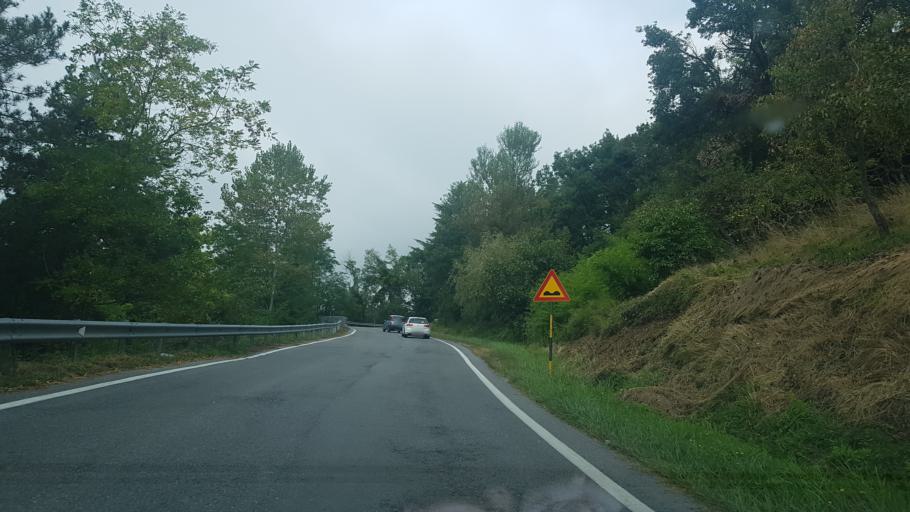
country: IT
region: Piedmont
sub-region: Provincia di Cuneo
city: Priero
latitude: 44.4009
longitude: 8.1096
